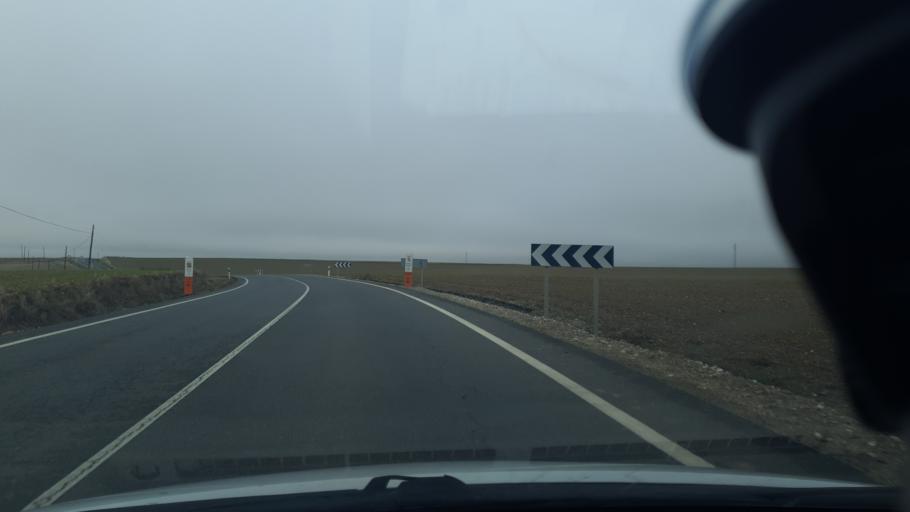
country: ES
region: Castille and Leon
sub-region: Provincia de Segovia
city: Encinillas
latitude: 41.0184
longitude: -4.1426
